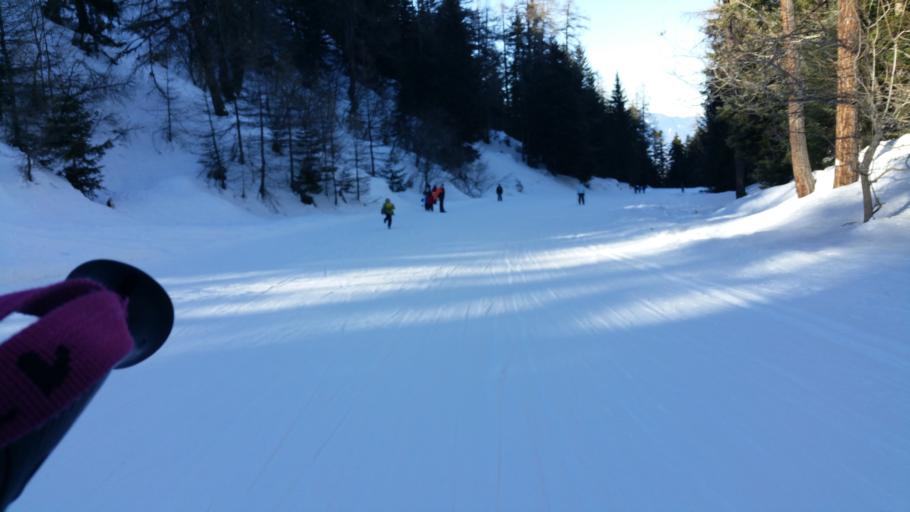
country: FR
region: Rhone-Alpes
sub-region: Departement de la Savoie
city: Valloire
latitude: 45.2210
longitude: 6.4125
